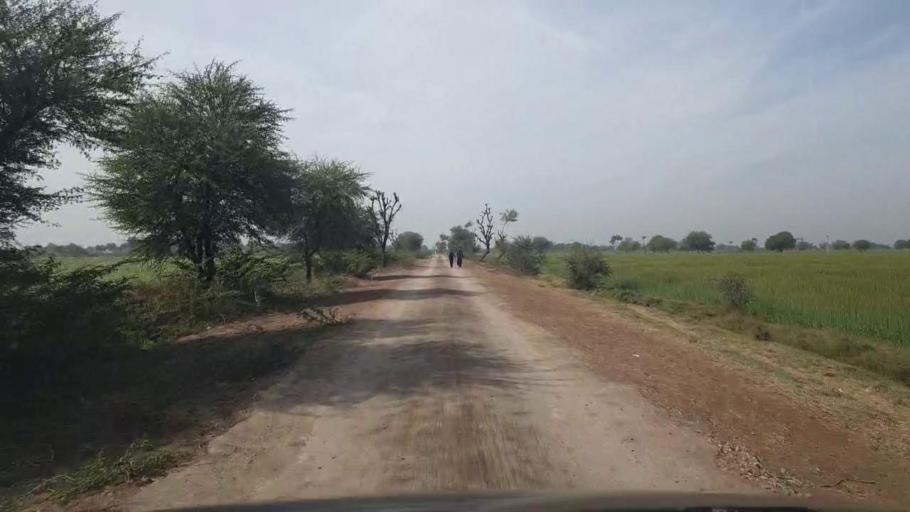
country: PK
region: Sindh
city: Umarkot
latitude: 25.3604
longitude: 69.6675
